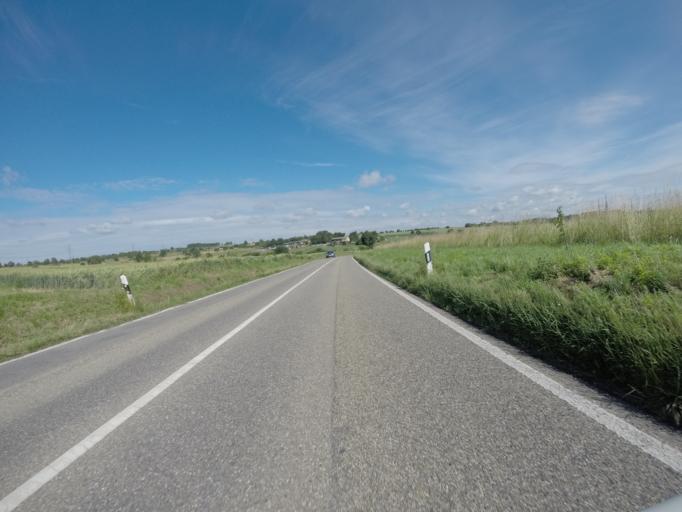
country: DE
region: Baden-Wuerttemberg
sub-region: Karlsruhe Region
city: Ettlingen
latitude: 48.9320
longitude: 8.4957
